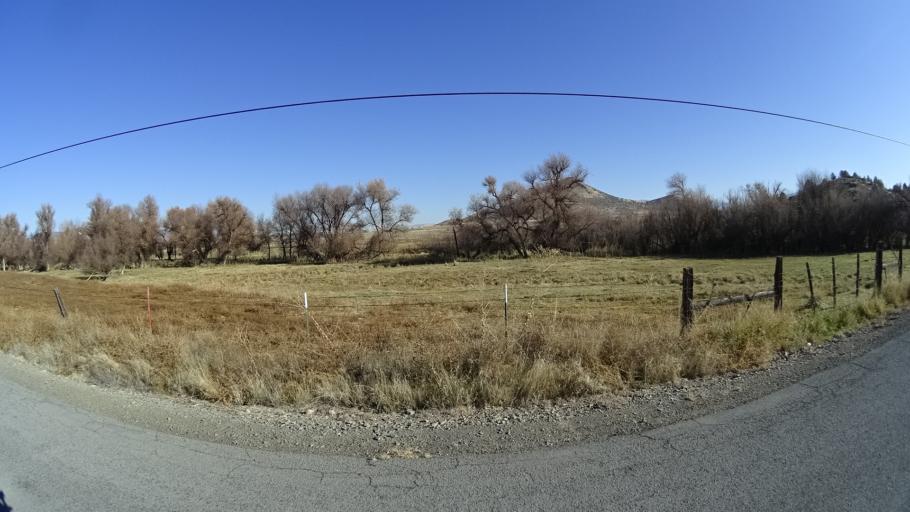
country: US
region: California
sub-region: Siskiyou County
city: Montague
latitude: 41.7029
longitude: -122.5354
